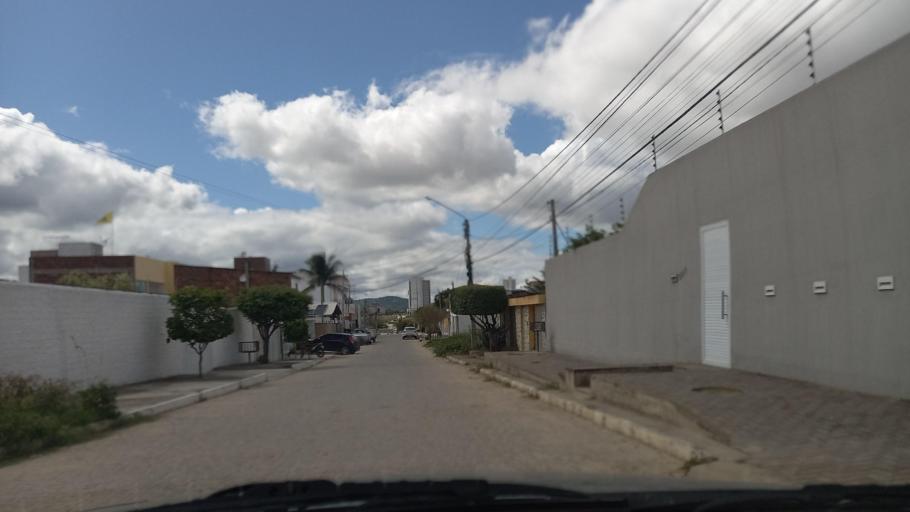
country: BR
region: Pernambuco
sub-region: Caruaru
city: Caruaru
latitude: -8.2578
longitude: -35.9790
